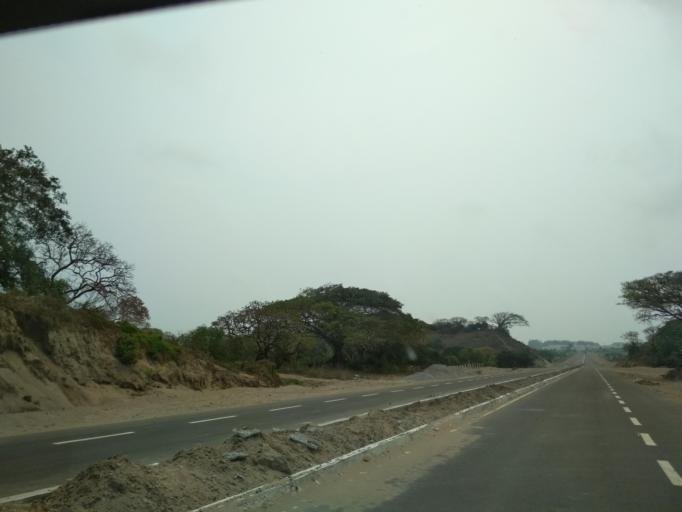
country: MX
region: Veracruz
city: Anton Lizardo
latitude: 19.0431
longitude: -95.9905
